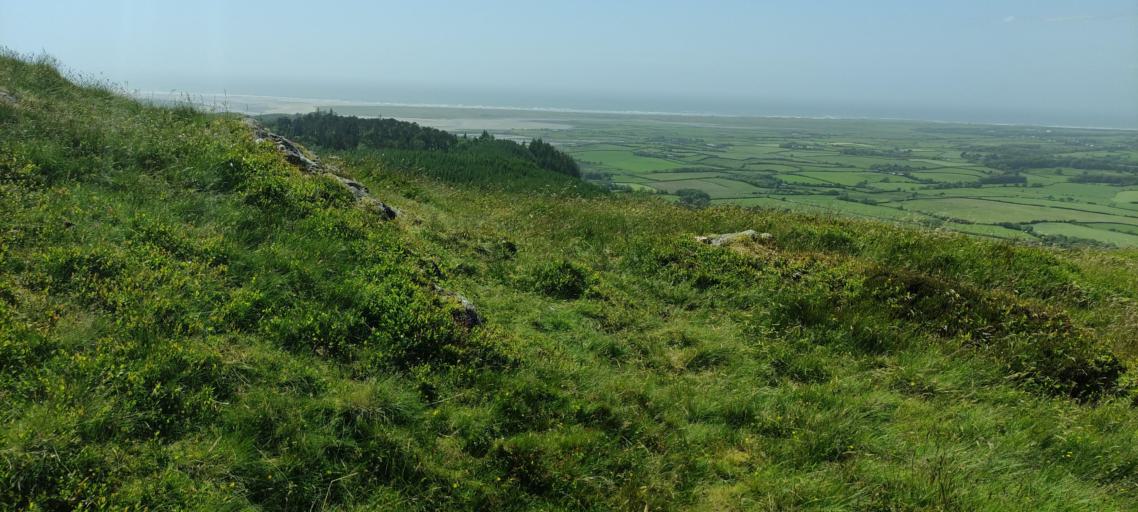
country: GB
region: England
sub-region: Cumbria
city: Seascale
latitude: 54.3727
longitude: -3.3684
